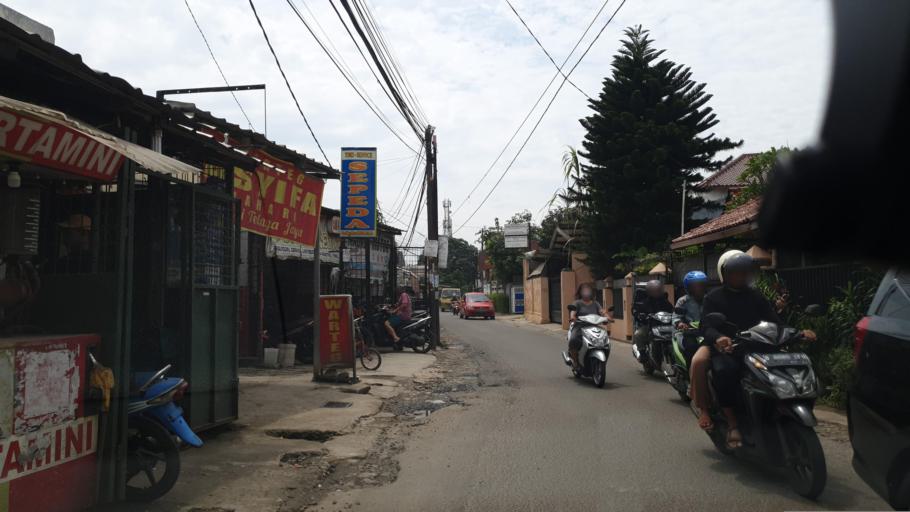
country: ID
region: West Java
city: Pamulang
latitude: -6.3631
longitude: 106.7620
